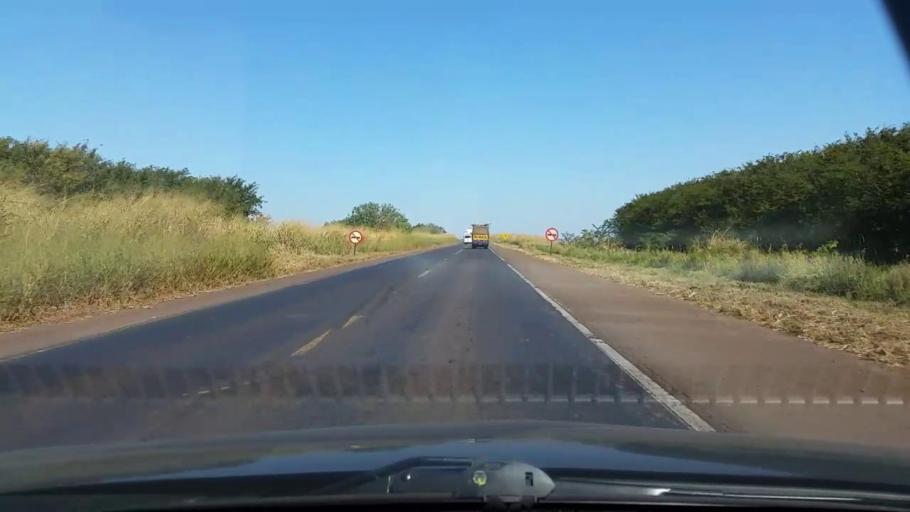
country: BR
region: Sao Paulo
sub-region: Igaracu Do Tiete
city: Igaracu do Tiete
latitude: -22.5596
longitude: -48.5624
